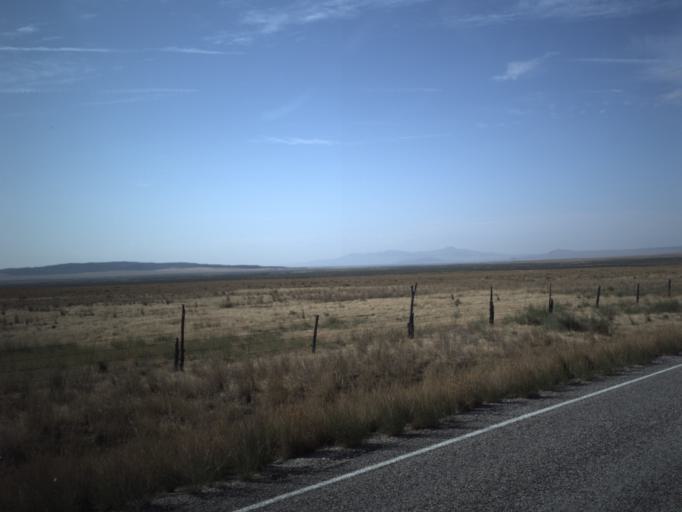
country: US
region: Idaho
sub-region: Oneida County
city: Malad City
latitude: 41.9632
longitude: -113.0633
